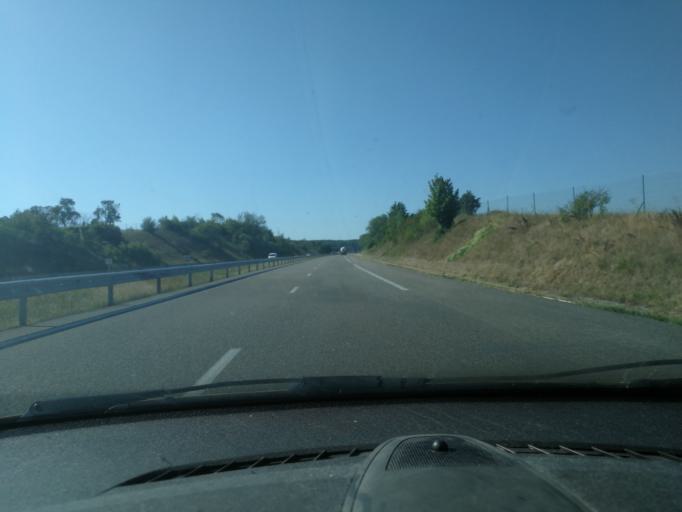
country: FR
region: Alsace
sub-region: Departement du Bas-Rhin
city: Sarrewerden
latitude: 48.9037
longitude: 7.1249
